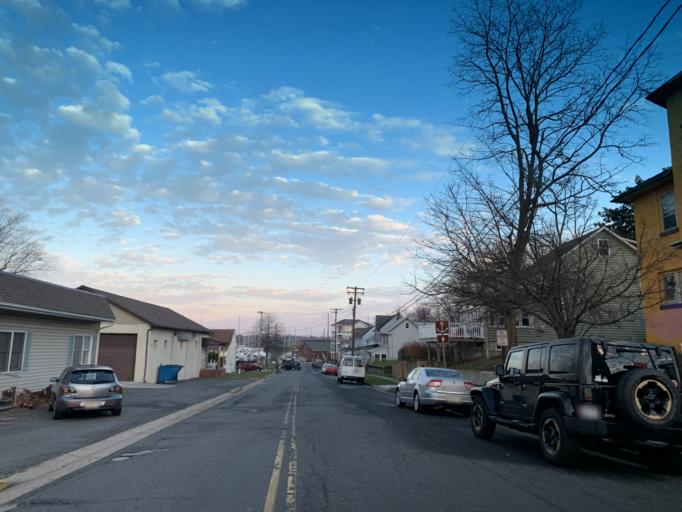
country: US
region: Maryland
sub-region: Harford County
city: Havre de Grace
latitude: 39.5551
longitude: -76.0954
